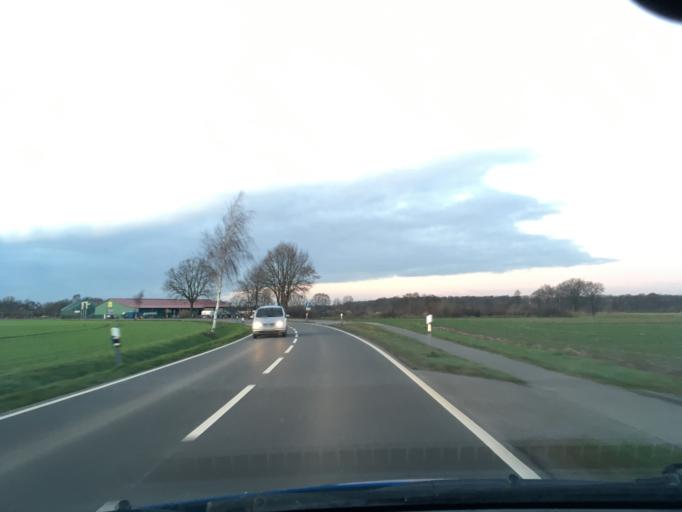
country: DE
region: Lower Saxony
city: Brietlingen
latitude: 53.3429
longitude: 10.4293
